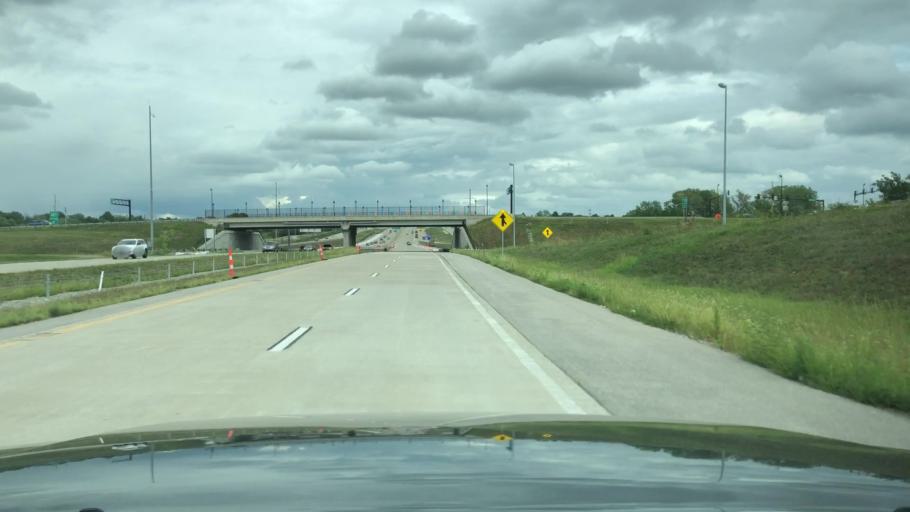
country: US
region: Missouri
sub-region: Saint Charles County
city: Cottleville
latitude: 38.7373
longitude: -90.6355
